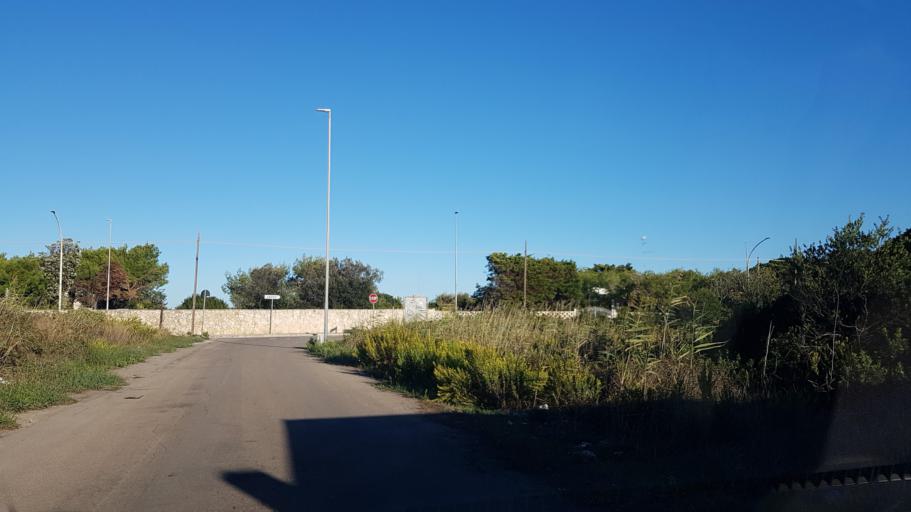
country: IT
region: Apulia
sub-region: Provincia di Lecce
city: Giorgilorio
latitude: 40.4648
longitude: 18.1945
